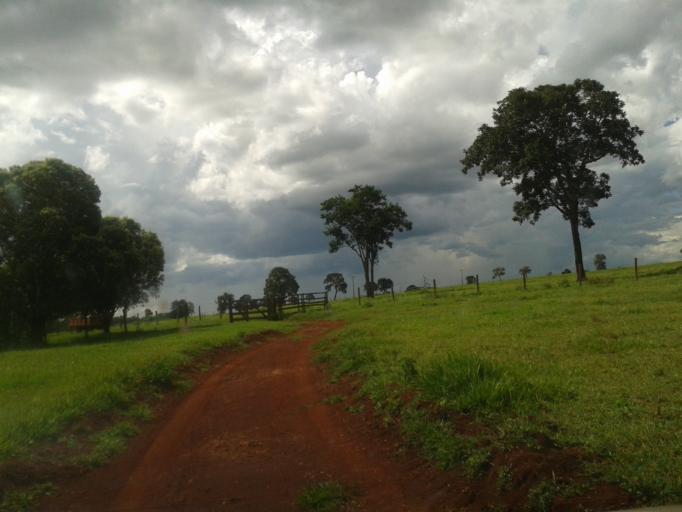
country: BR
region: Minas Gerais
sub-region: Capinopolis
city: Capinopolis
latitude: -18.7635
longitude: -49.8248
